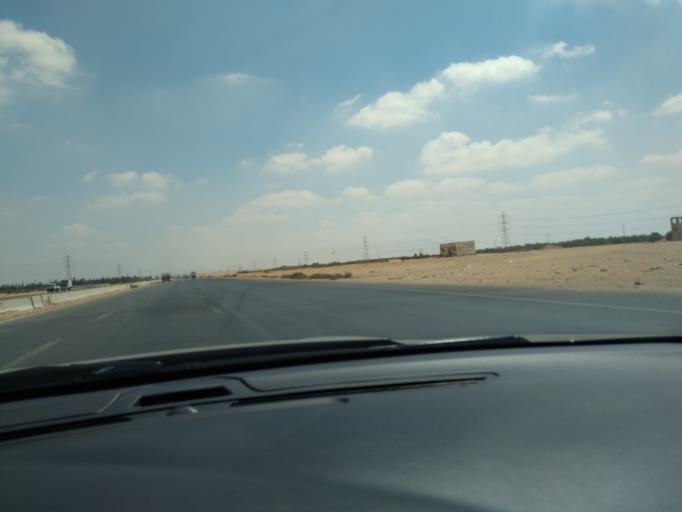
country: EG
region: Al Isma'iliyah
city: At Tall al Kabir
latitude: 30.3529
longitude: 31.8895
